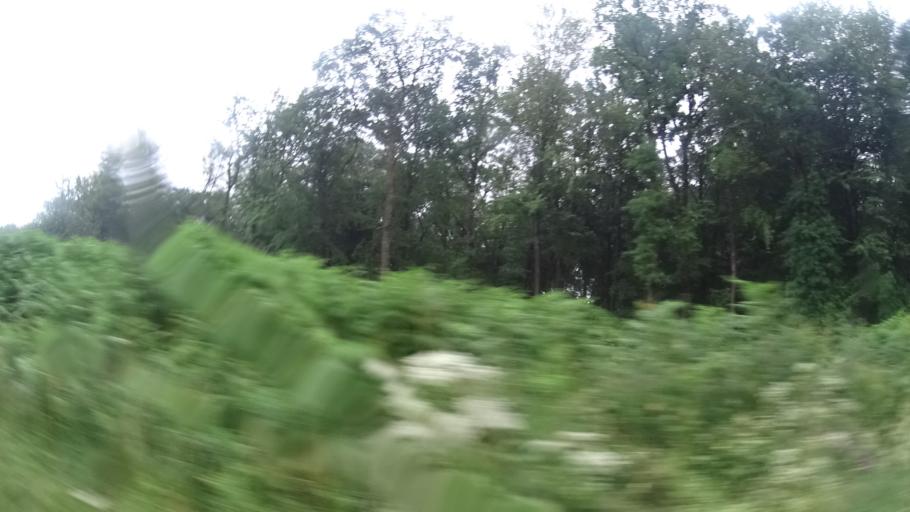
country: BE
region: Wallonia
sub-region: Province du Luxembourg
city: Paliseul
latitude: 49.9332
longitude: 5.0814
